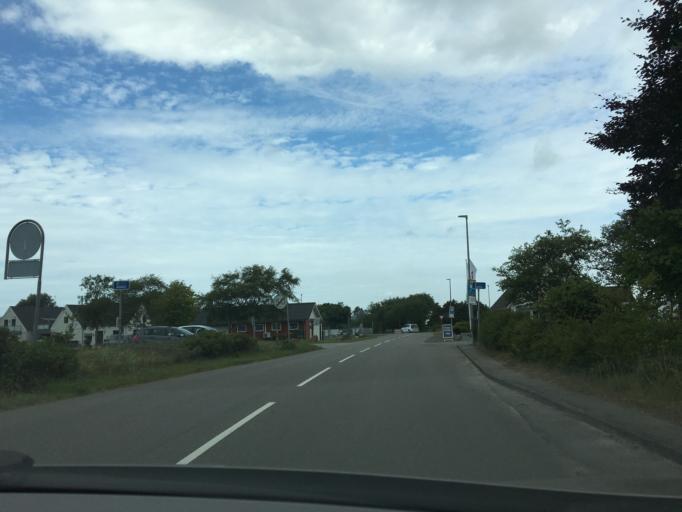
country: DK
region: South Denmark
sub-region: Varde Kommune
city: Oksbol
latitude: 55.7888
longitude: 8.2401
